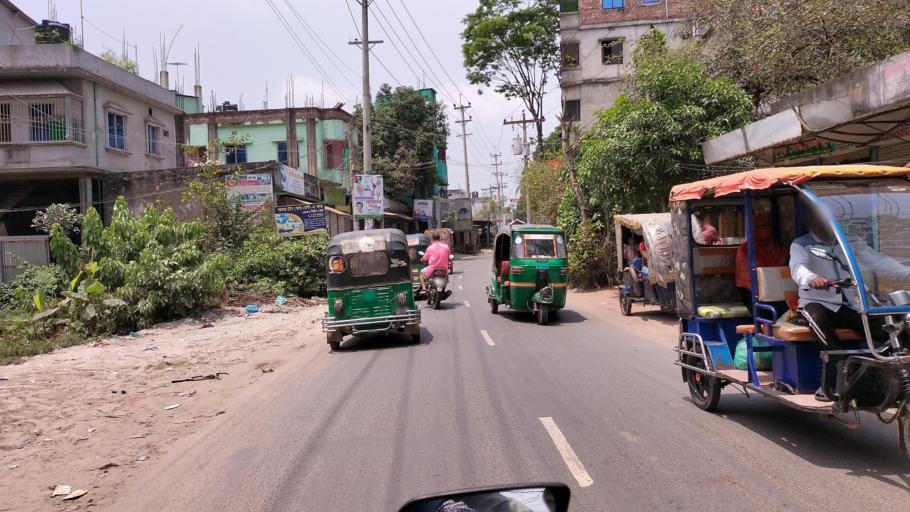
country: BD
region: Dhaka
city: Azimpur
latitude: 23.7305
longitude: 90.2773
